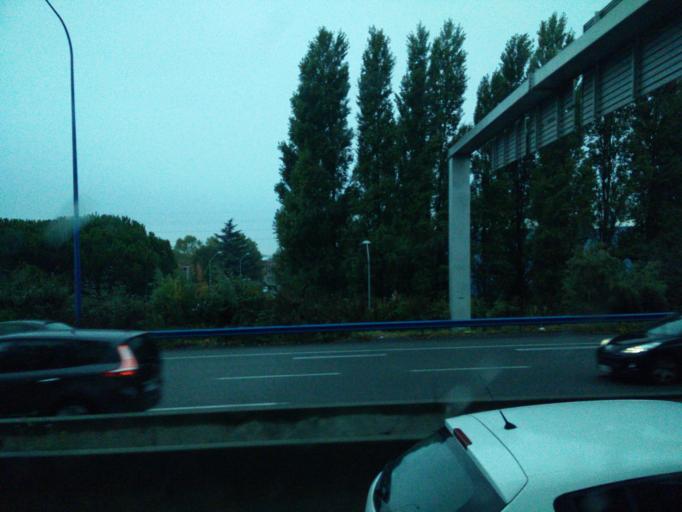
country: FR
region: Midi-Pyrenees
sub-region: Departement de la Haute-Garonne
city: Blagnac
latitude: 43.6277
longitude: 1.4201
